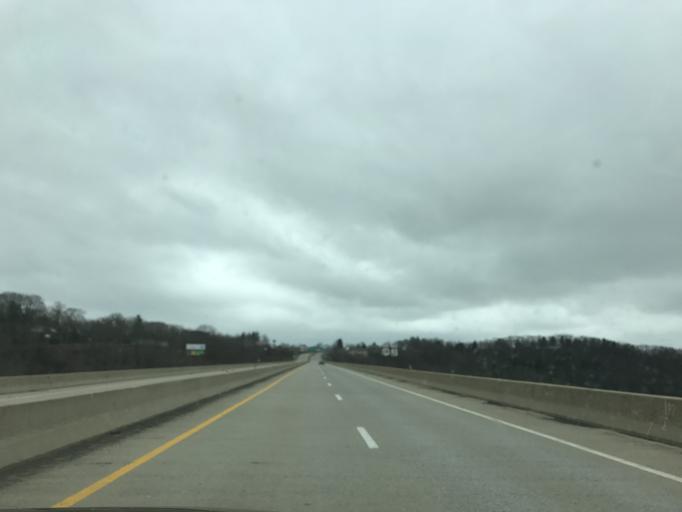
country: US
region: West Virginia
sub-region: Raleigh County
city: Beaver
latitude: 37.7650
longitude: -81.1521
